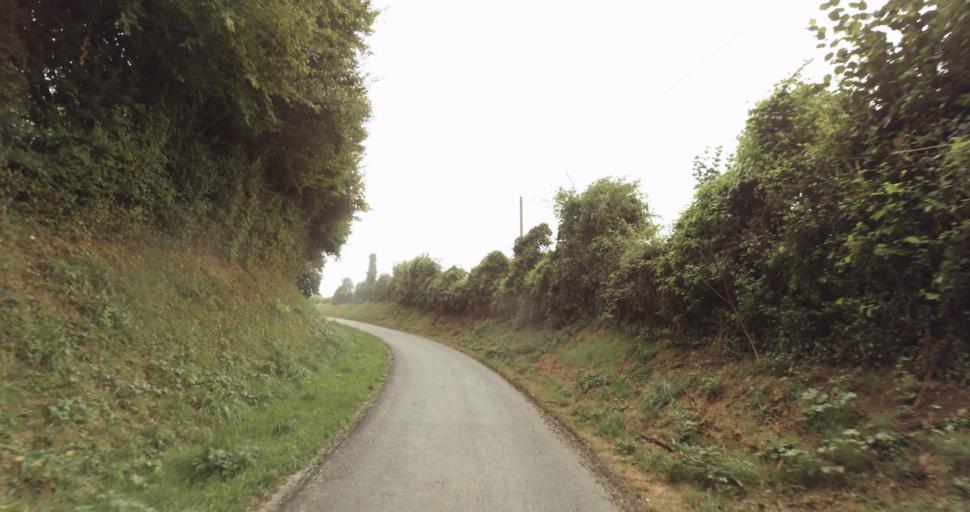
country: FR
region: Lower Normandy
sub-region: Departement de l'Orne
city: Gace
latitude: 48.8841
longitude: 0.2833
